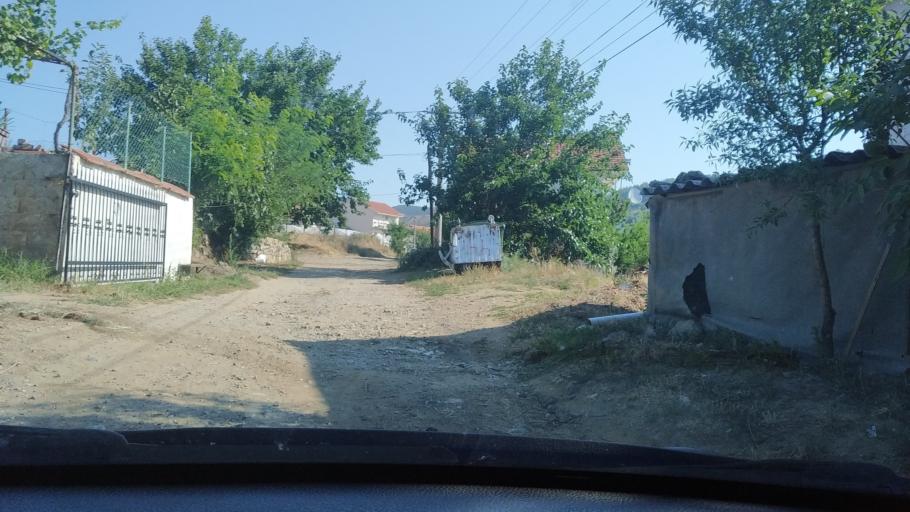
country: MK
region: Bogdanci
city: Bogdanci
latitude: 41.2057
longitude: 22.5821
